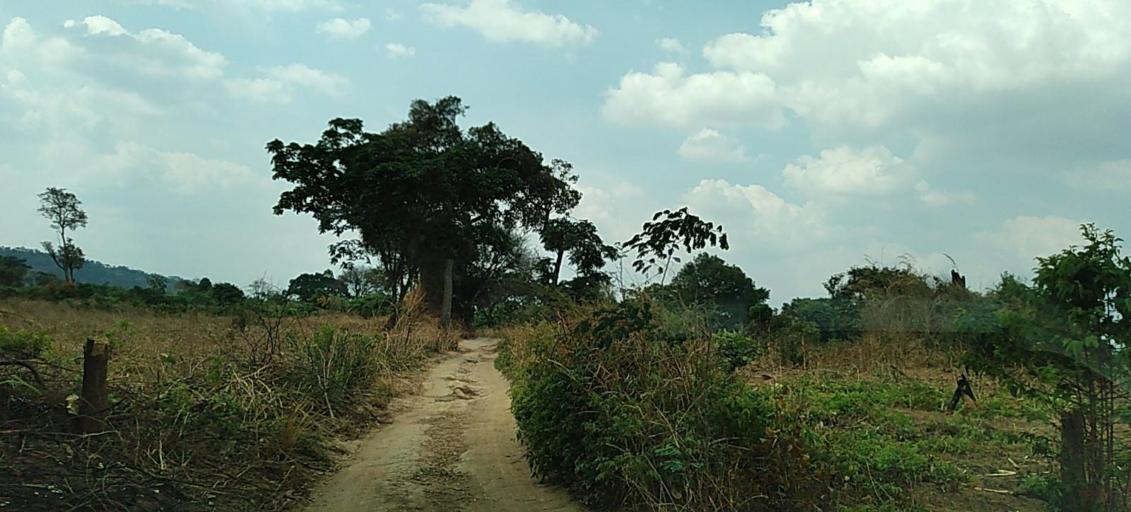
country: ZM
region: Copperbelt
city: Chililabombwe
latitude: -12.3264
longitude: 27.7484
